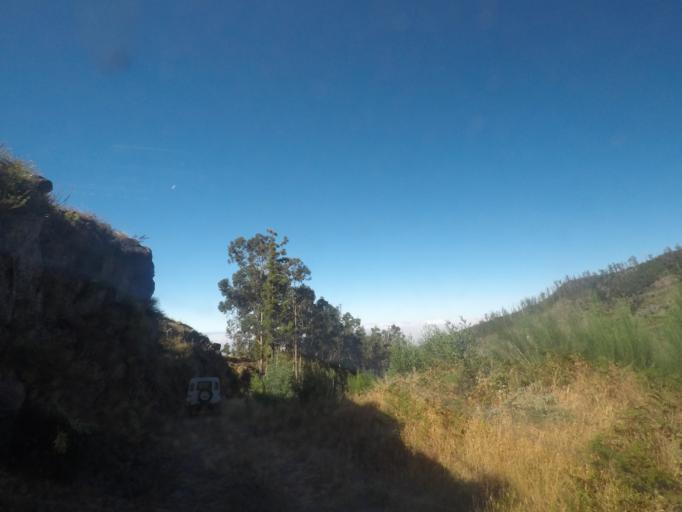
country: PT
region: Madeira
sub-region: Funchal
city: Nossa Senhora do Monte
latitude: 32.6941
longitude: -16.9117
